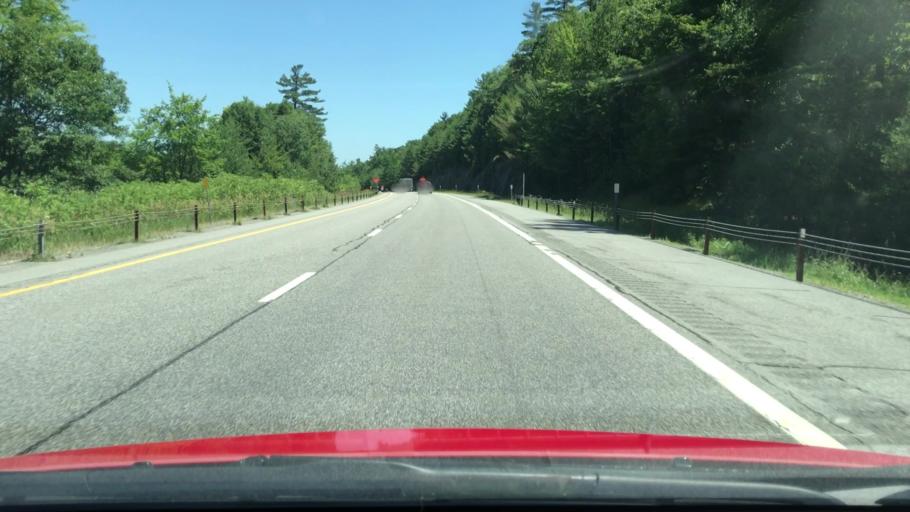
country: US
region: New York
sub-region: Essex County
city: Elizabethtown
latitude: 44.2001
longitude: -73.5148
